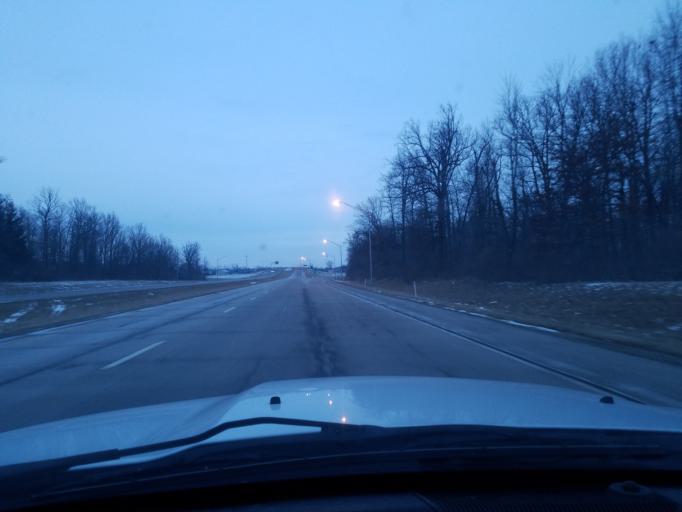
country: US
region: Indiana
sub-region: Delaware County
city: Muncie
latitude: 40.1986
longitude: -85.3364
